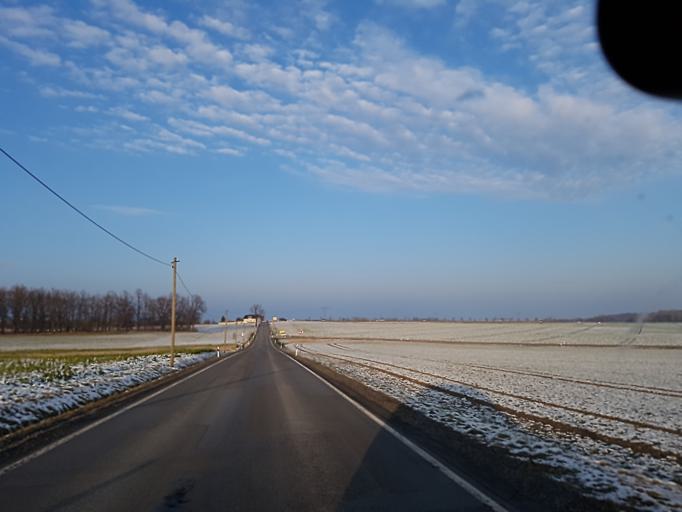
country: DE
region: Saxony
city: Oschatz
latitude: 51.2773
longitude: 13.1256
